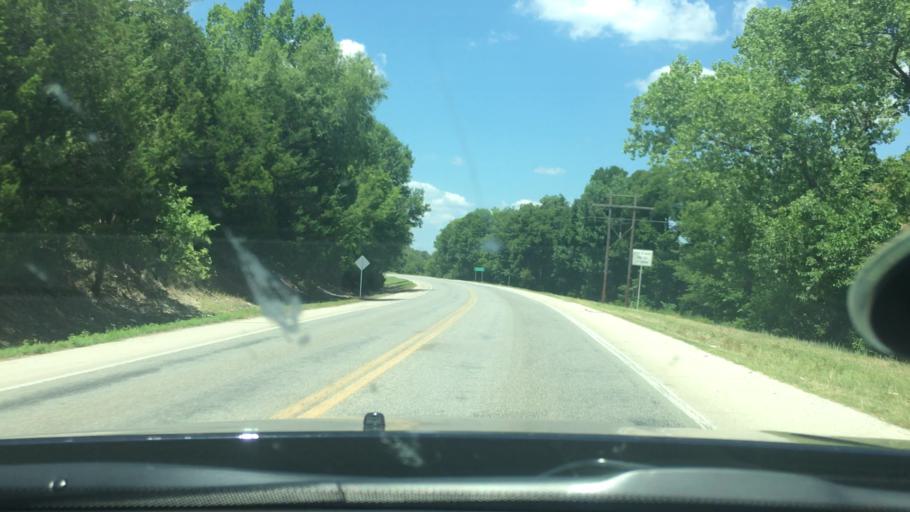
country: US
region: Oklahoma
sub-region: Marshall County
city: Oakland
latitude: 34.1727
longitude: -96.8381
